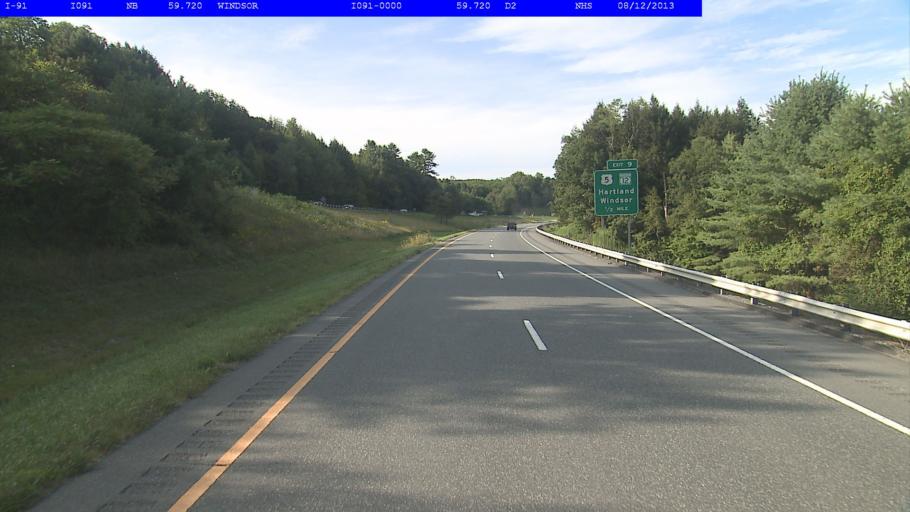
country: US
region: Vermont
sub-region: Windsor County
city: Windsor
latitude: 43.5186
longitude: -72.4085
